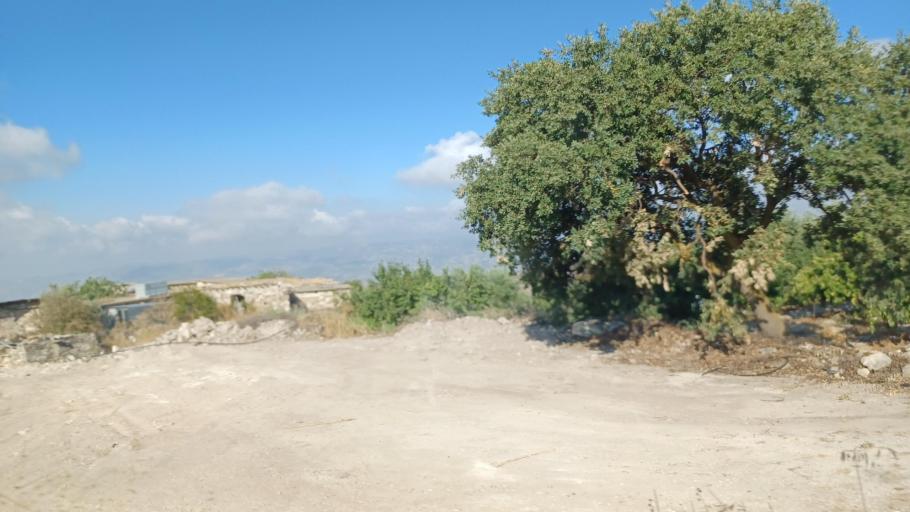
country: CY
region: Pafos
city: Mesogi
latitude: 34.8732
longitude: 32.6111
